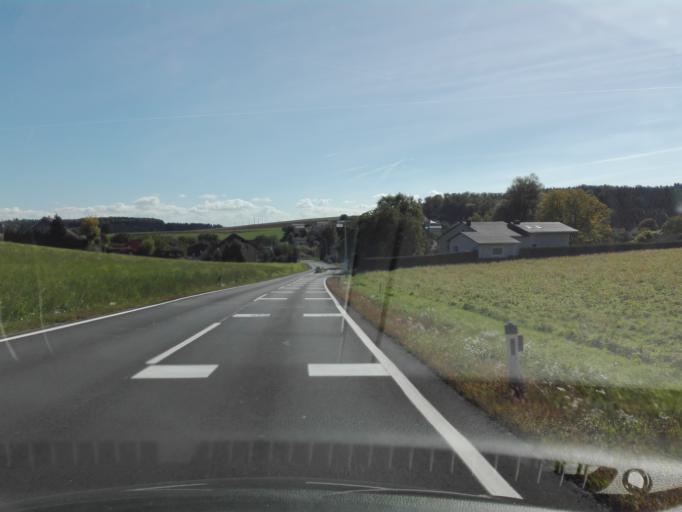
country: AT
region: Upper Austria
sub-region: Politischer Bezirk Linz-Land
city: Sankt Florian
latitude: 48.2179
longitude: 14.3460
